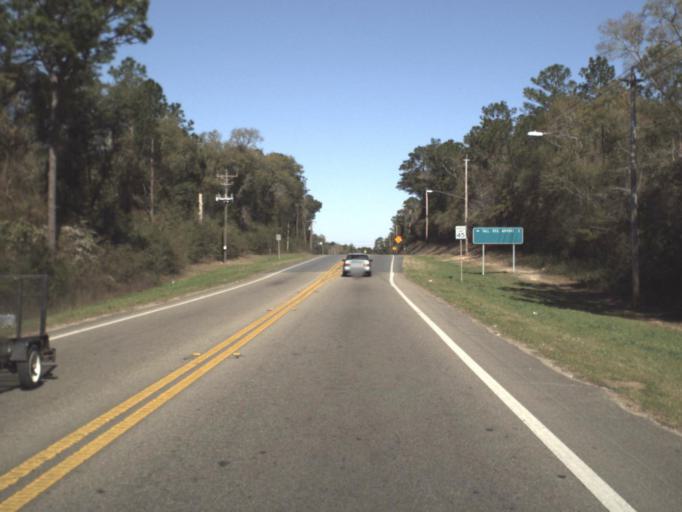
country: US
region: Florida
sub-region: Leon County
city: Tallahassee
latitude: 30.4163
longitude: -84.3463
